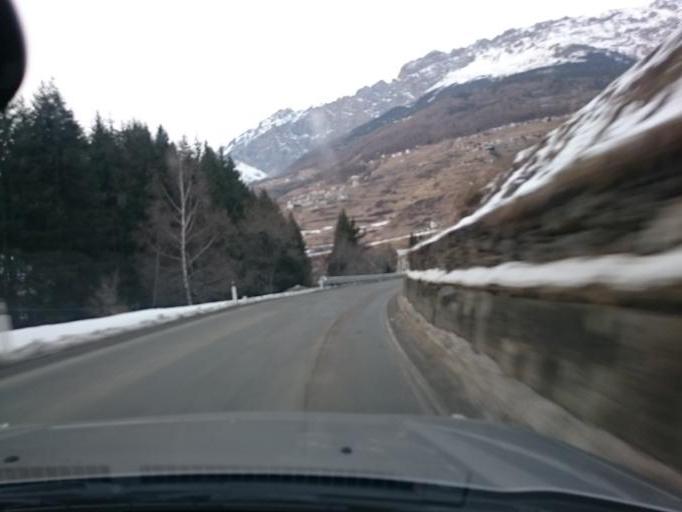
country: IT
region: Lombardy
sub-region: Provincia di Sondrio
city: Sant'Antonio
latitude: 46.4538
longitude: 10.4320
